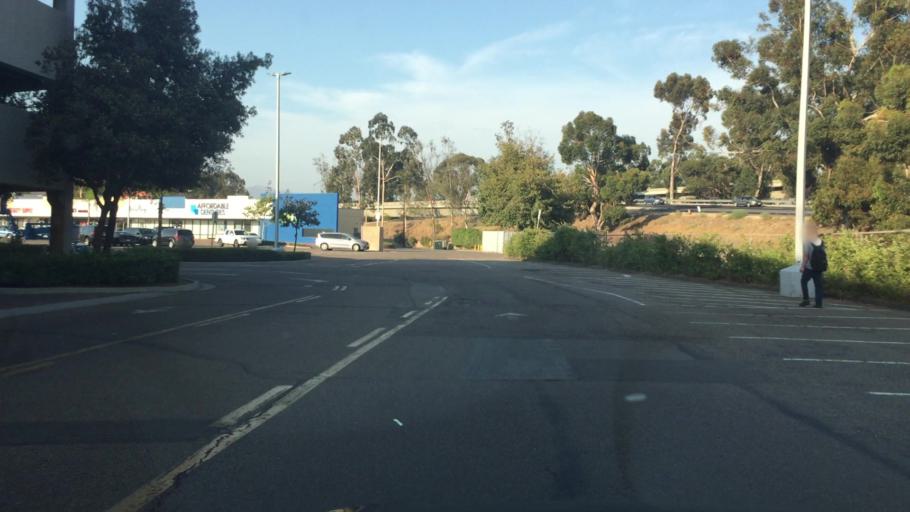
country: US
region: California
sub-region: San Diego County
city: El Cajon
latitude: 32.8042
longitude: -116.9644
